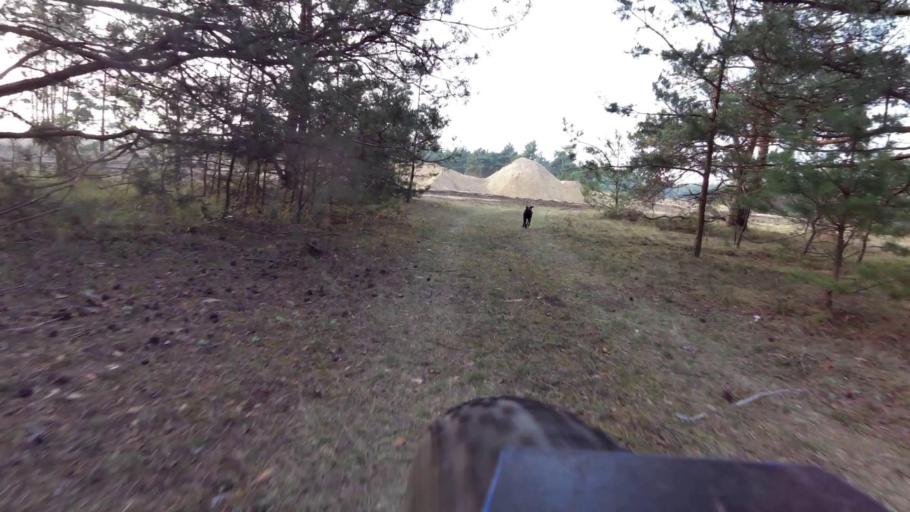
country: DE
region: Brandenburg
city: Ziltendorf
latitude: 52.2725
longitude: 14.6871
